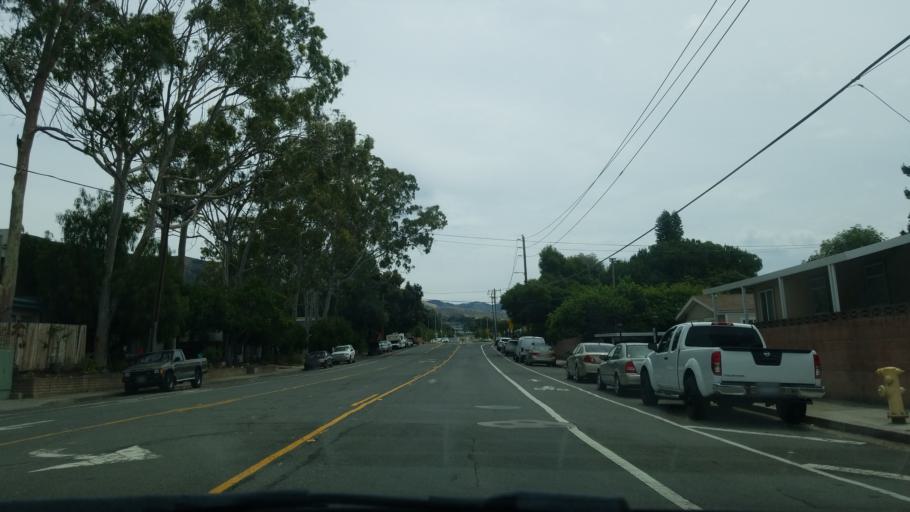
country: US
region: California
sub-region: San Luis Obispo County
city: San Luis Obispo
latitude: 35.2614
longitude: -120.6422
